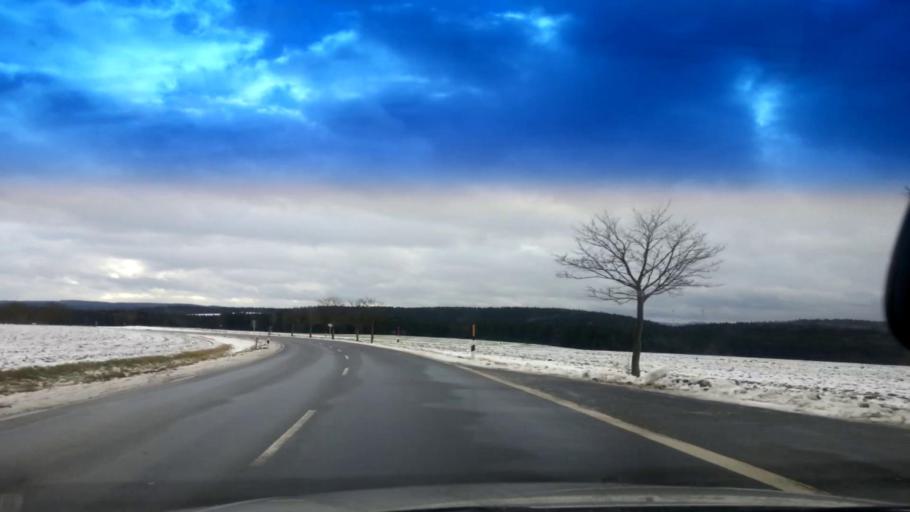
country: DE
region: Bavaria
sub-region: Upper Franconia
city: Kirchenlamitz
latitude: 50.1377
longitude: 11.9697
